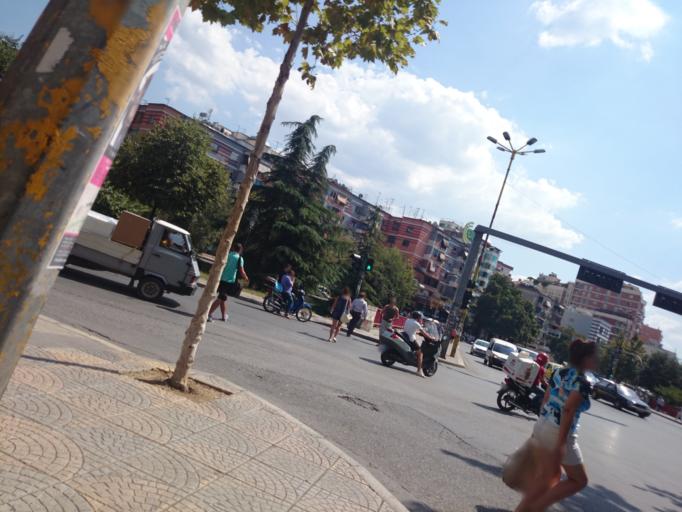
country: AL
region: Tirane
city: Tirana
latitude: 41.3257
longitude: 19.8250
